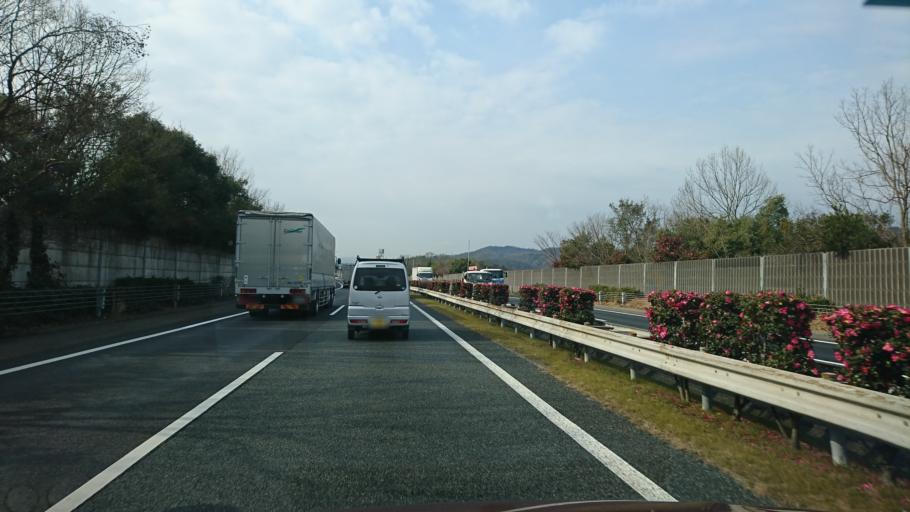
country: JP
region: Hiroshima
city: Kannabecho-yahiro
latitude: 34.5382
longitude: 133.4619
